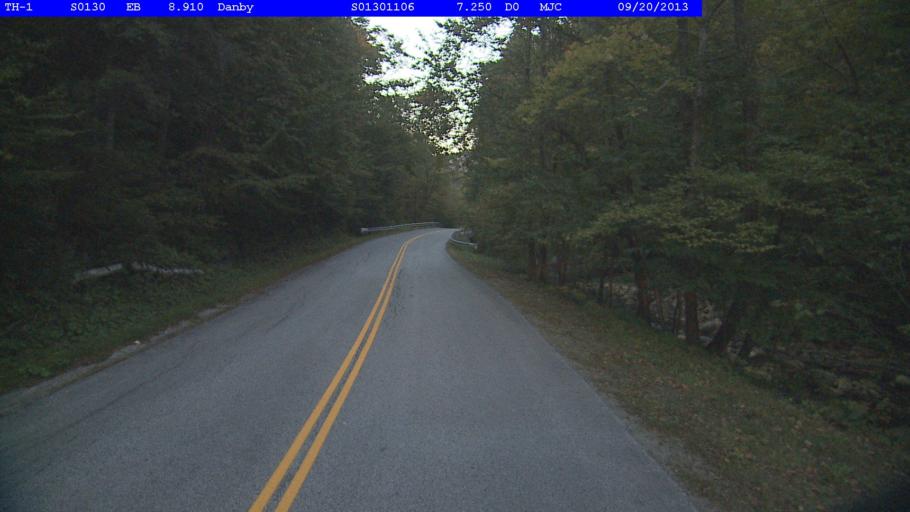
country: US
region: Vermont
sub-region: Bennington County
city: Manchester Center
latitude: 43.3386
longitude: -73.0139
